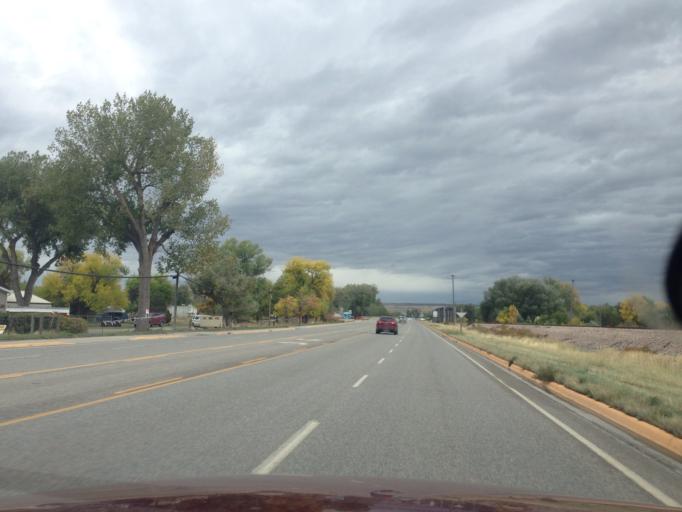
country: US
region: Montana
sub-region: Yellowstone County
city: Laurel
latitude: 45.6567
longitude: -108.7629
